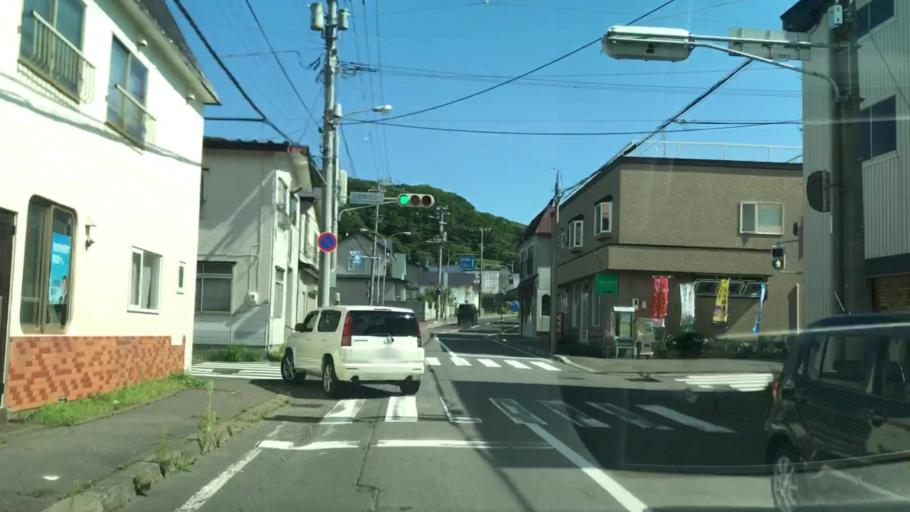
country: JP
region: Hokkaido
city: Muroran
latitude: 42.3104
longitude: 140.9966
